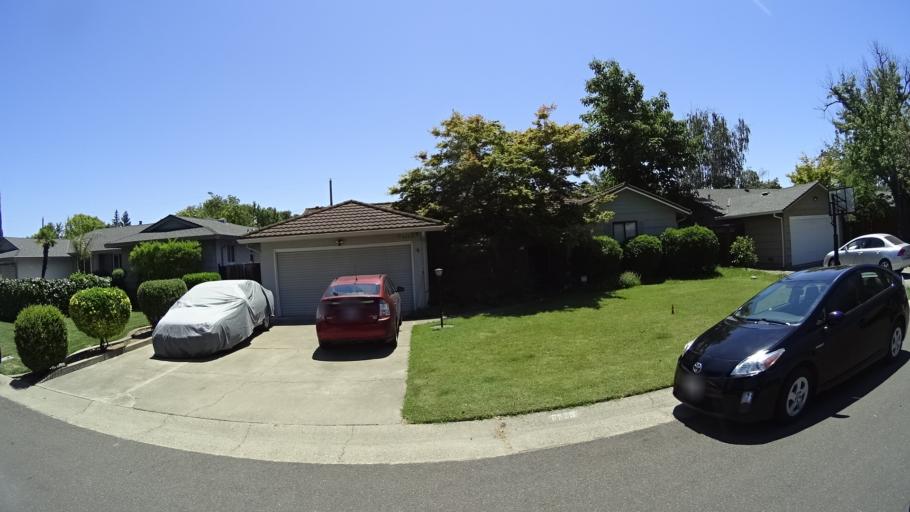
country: US
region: California
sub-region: Sacramento County
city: Sacramento
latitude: 38.5380
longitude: -121.5096
